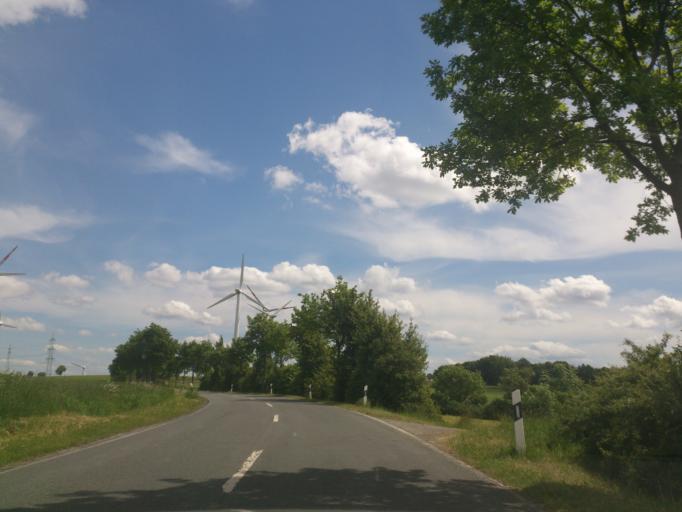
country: DE
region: North Rhine-Westphalia
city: Beverungen
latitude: 51.6297
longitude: 9.3382
